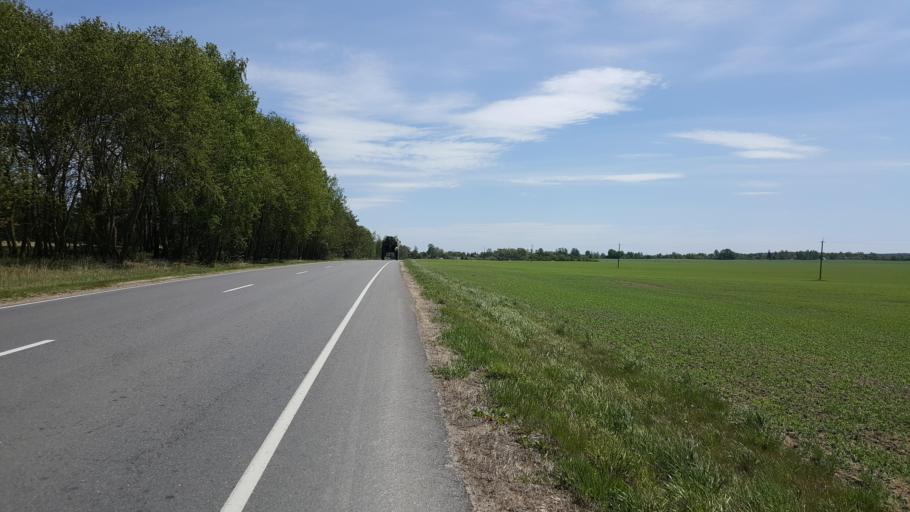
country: BY
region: Brest
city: Zhabinka
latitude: 52.3571
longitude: 24.1704
